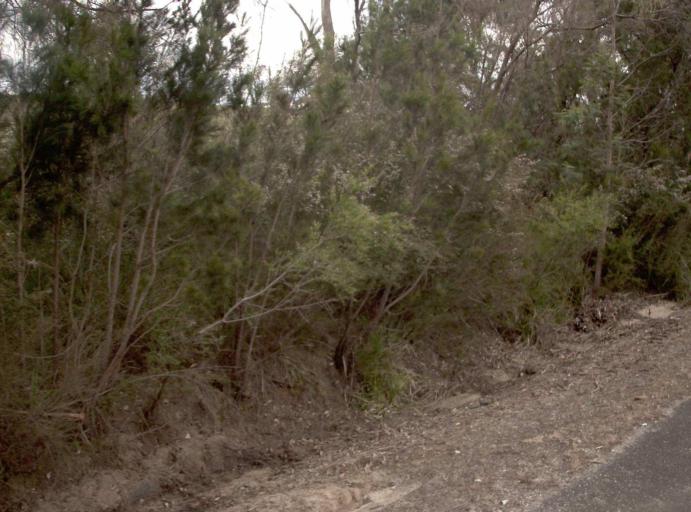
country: AU
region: Victoria
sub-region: Wellington
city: Sale
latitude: -38.2063
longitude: 147.0706
